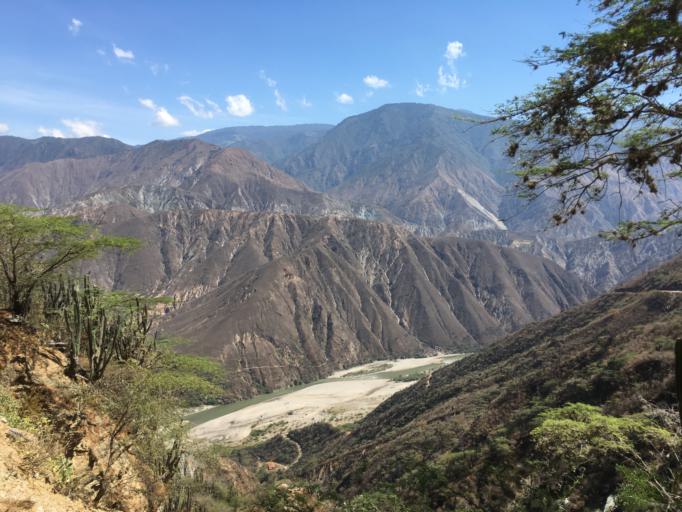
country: CO
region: Santander
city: Aratoca
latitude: 6.7724
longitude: -72.9943
